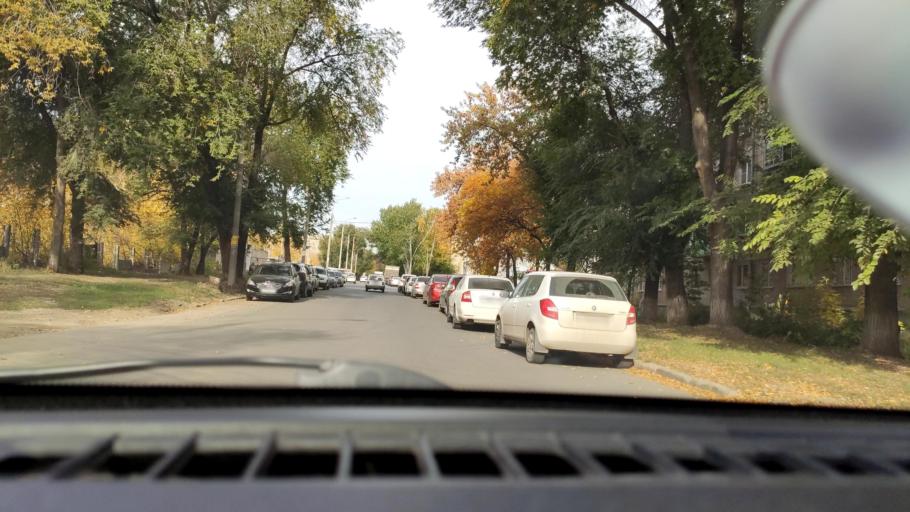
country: RU
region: Samara
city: Samara
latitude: 53.2148
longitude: 50.2313
